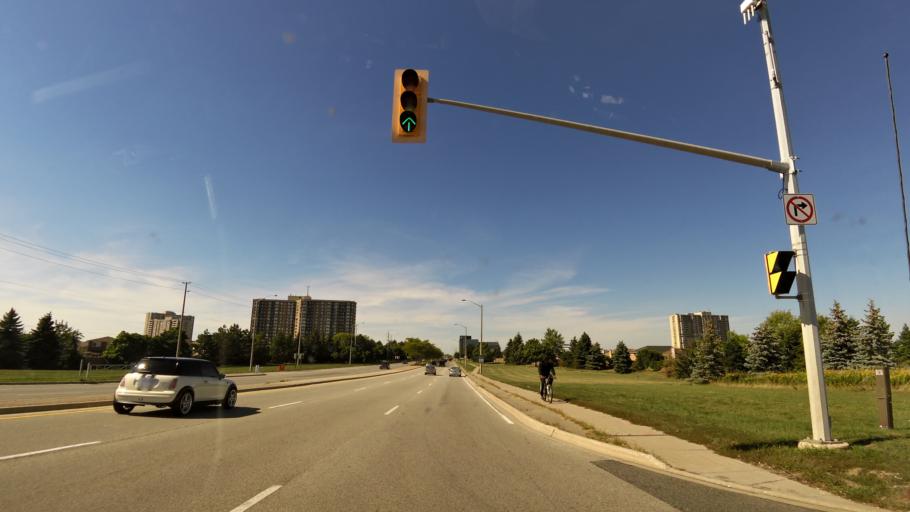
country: CA
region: Ontario
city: Brampton
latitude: 43.6548
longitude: -79.7180
